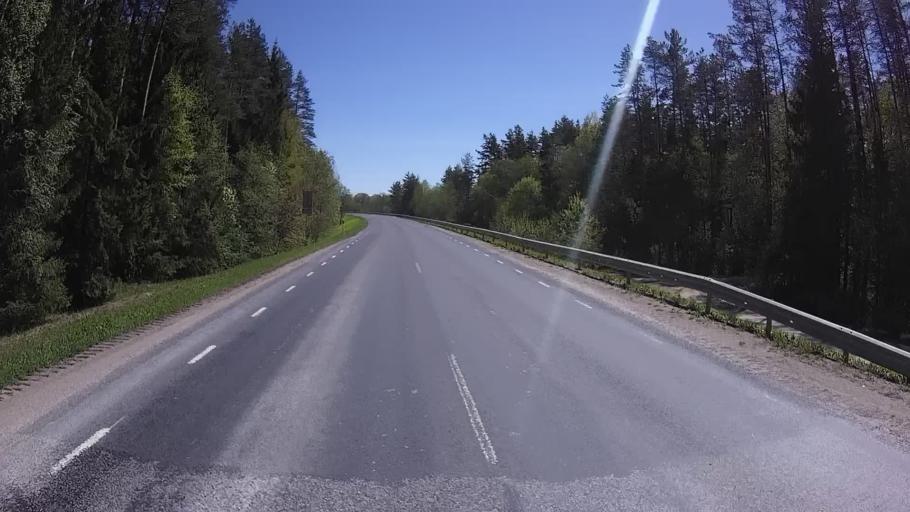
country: EE
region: Harju
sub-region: Raasiku vald
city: Raasiku
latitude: 59.1597
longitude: 25.1836
